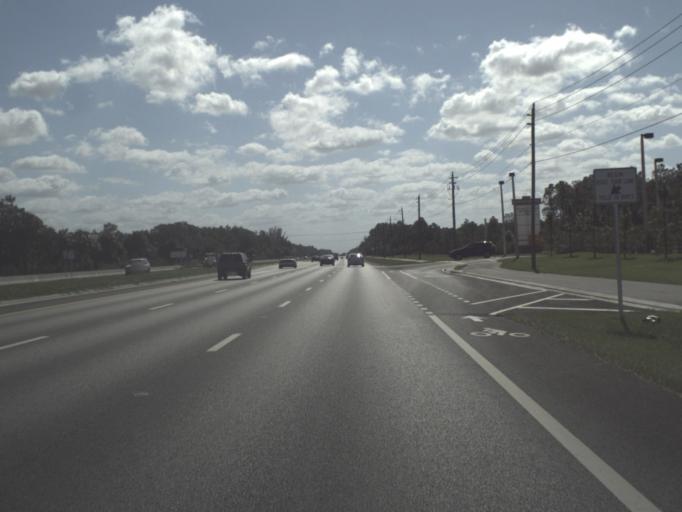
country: US
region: Florida
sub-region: Collier County
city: Lely Resort
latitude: 26.0613
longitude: -81.6964
